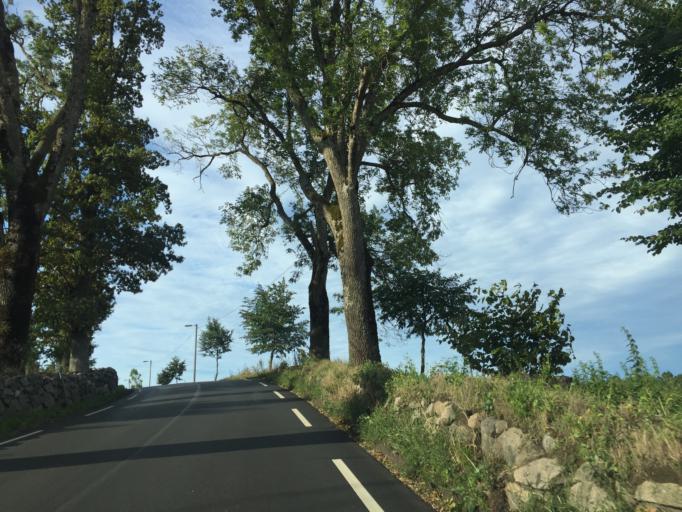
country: NO
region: Akershus
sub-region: As
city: As
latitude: 59.7151
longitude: 10.7742
